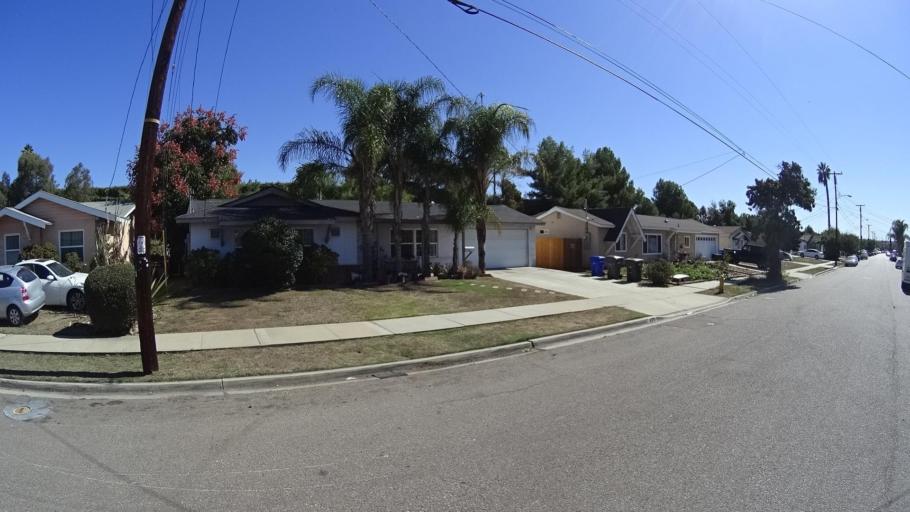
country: US
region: California
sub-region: San Diego County
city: La Presa
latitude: 32.7129
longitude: -117.0150
